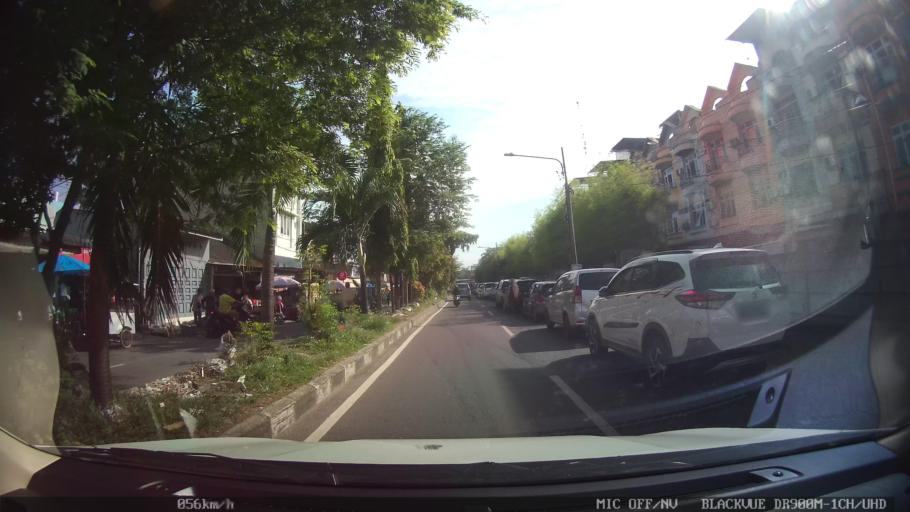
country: ID
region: North Sumatra
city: Medan
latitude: 3.5940
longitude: 98.6614
